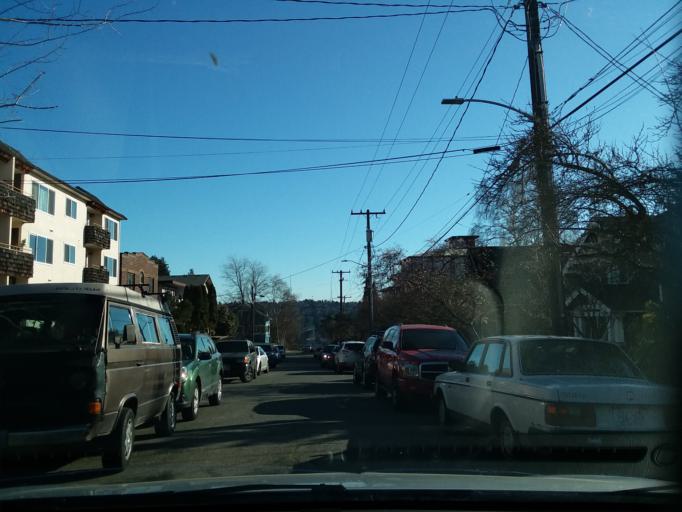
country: US
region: Washington
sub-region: King County
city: Seattle
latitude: 47.6587
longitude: -122.3544
